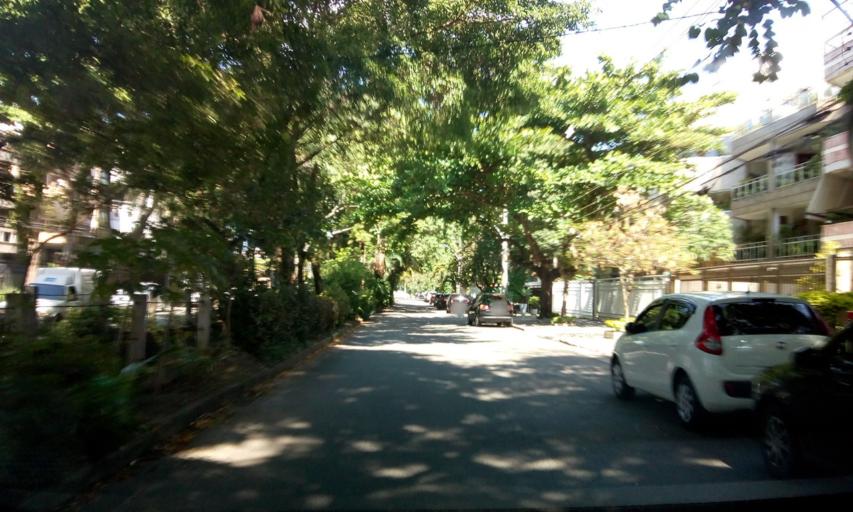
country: BR
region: Rio de Janeiro
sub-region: Rio De Janeiro
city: Rio de Janeiro
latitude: -23.0115
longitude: -43.3069
